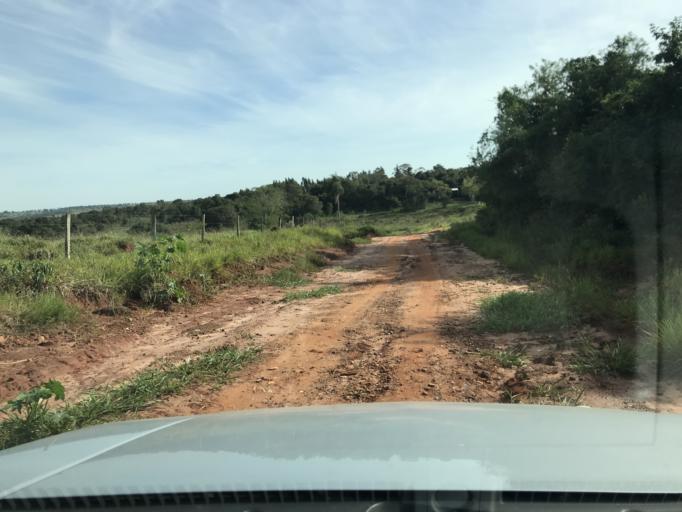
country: BR
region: Mato Grosso do Sul
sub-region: Iguatemi
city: Iguatemi
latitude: -23.6475
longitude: -54.5761
